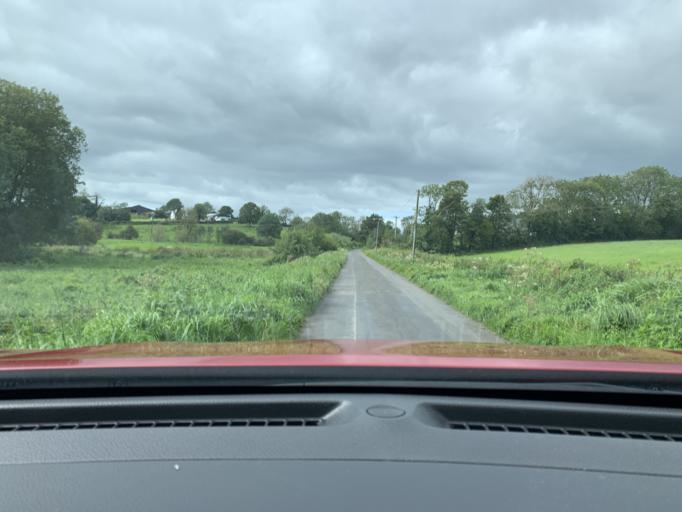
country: IE
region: Connaught
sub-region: Sligo
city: Collooney
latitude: 54.1579
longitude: -8.4288
